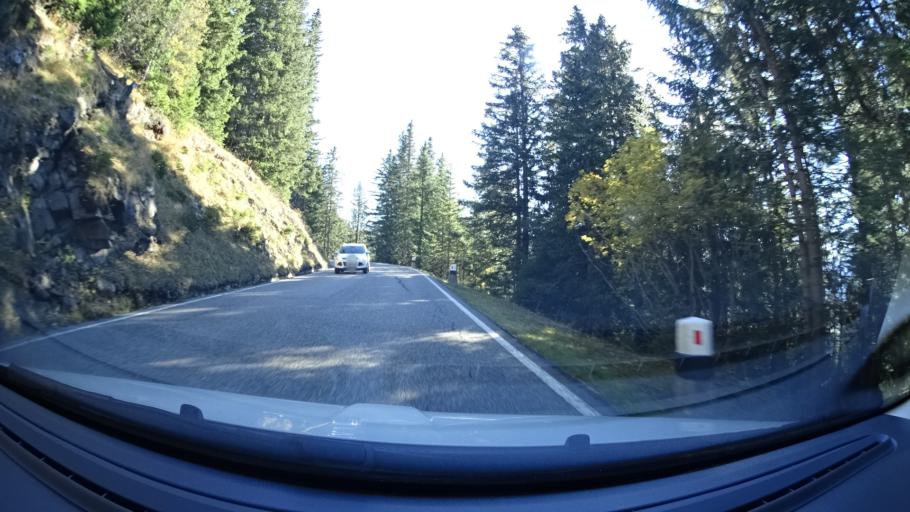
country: IT
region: Trentino-Alto Adige
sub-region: Provincia di Trento
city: Canazei
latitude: 46.4840
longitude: 11.7870
